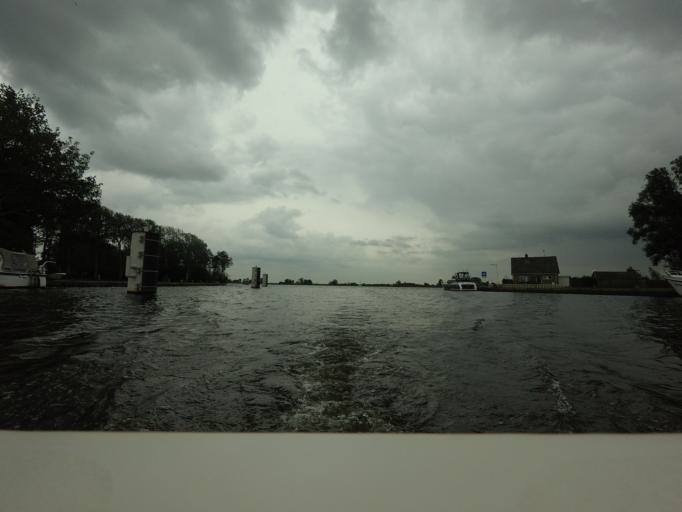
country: NL
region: Friesland
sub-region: Gemeente Smallingerland
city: Oudega
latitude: 53.1046
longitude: 5.9500
